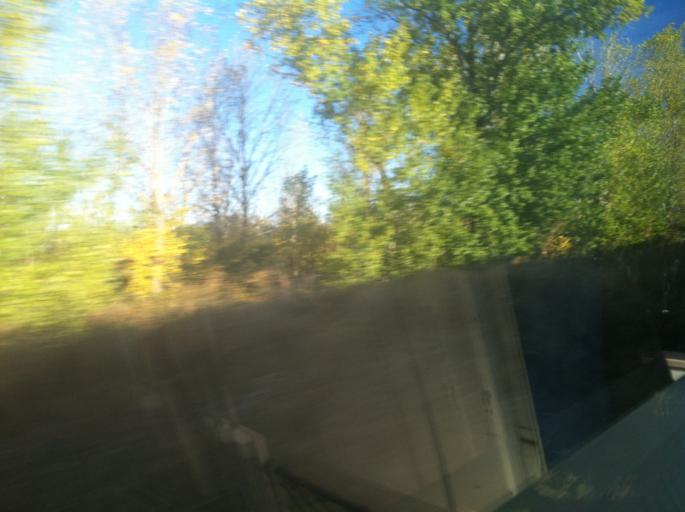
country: ES
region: Castille and Leon
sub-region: Provincia de Valladolid
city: Cabezon
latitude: 41.7640
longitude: -4.6255
